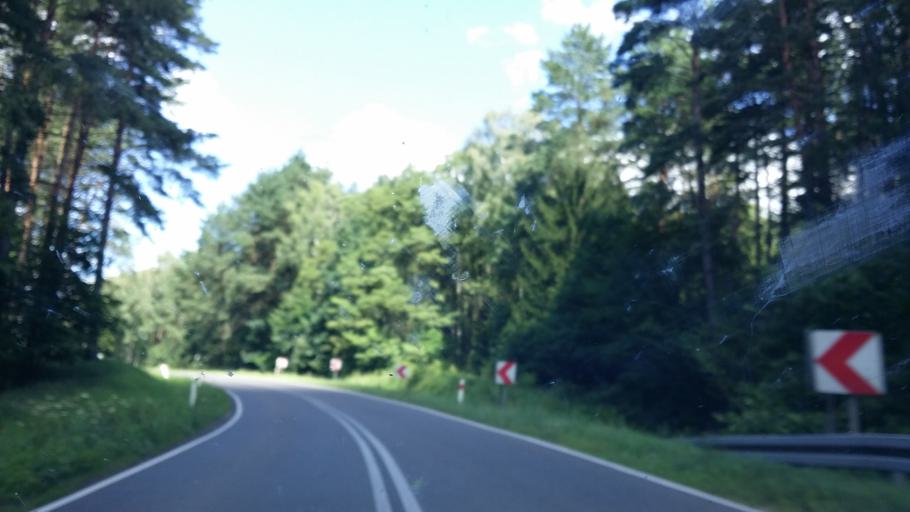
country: PL
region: West Pomeranian Voivodeship
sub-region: Powiat swidwinski
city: Slawoborze
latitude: 53.8761
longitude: 15.7285
